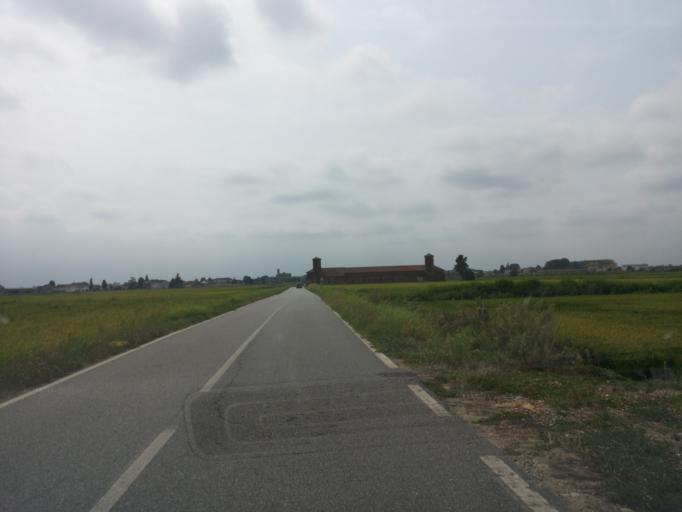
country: IT
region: Piedmont
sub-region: Provincia di Vercelli
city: Prarolo
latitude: 45.2727
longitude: 8.4828
